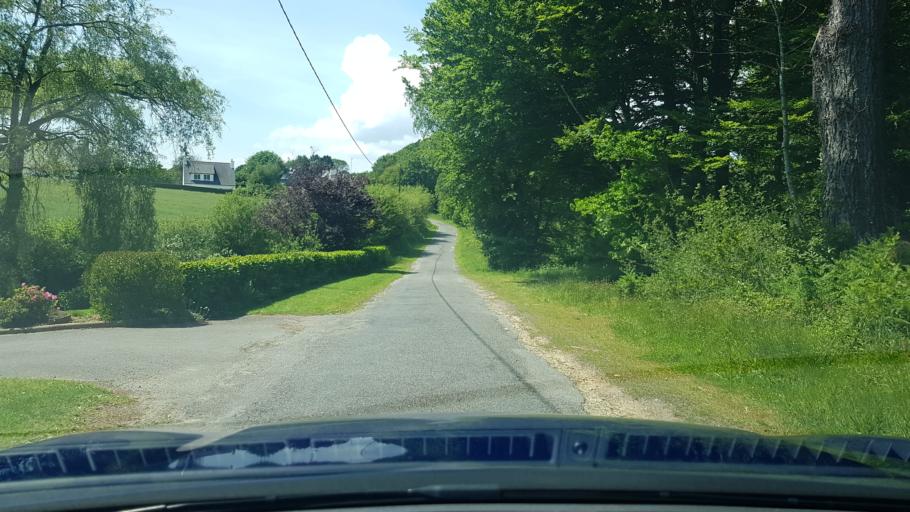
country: FR
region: Brittany
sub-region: Departement du Morbihan
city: Gestel
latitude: 47.8015
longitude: -3.4868
